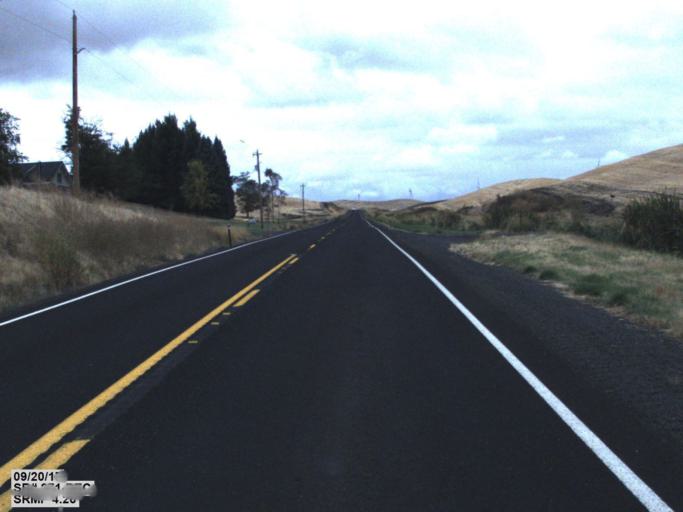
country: US
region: Washington
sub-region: Whitman County
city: Colfax
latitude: 47.1802
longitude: -117.2937
